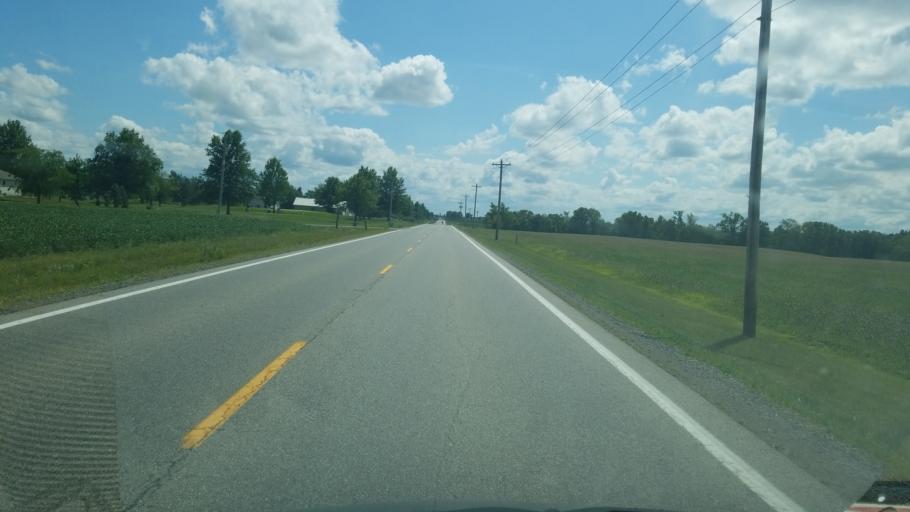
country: US
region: Ohio
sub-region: Putnam County
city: Kalida
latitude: 41.0362
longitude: -84.1981
